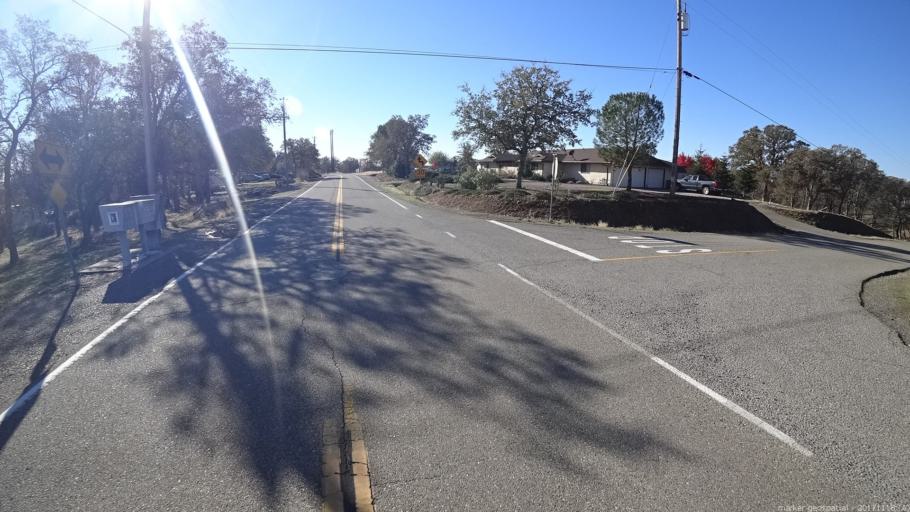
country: US
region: California
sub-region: Shasta County
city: Cottonwood
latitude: 40.3949
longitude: -122.3144
